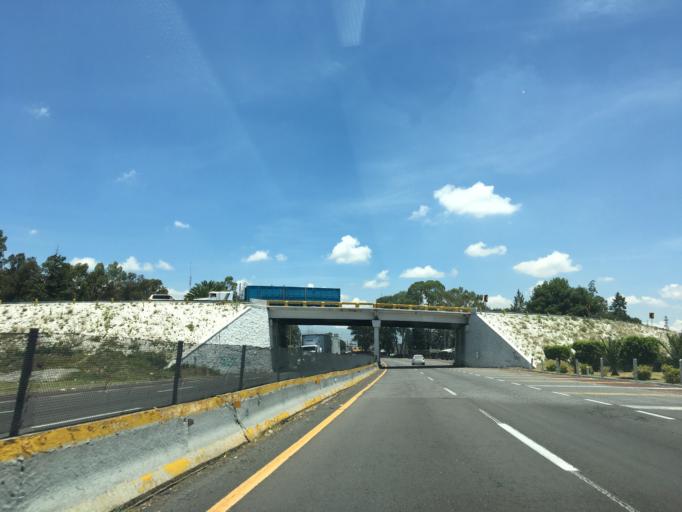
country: MX
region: Puebla
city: San Martin Texmelucan de Labastida
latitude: 19.2699
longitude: -98.4278
